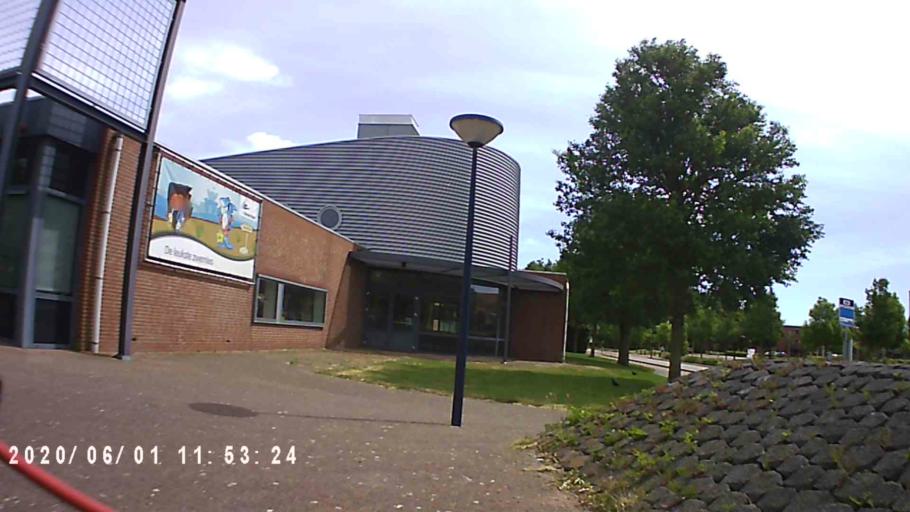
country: NL
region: Friesland
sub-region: Gemeente Harlingen
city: Harlingen
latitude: 53.1633
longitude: 5.4281
